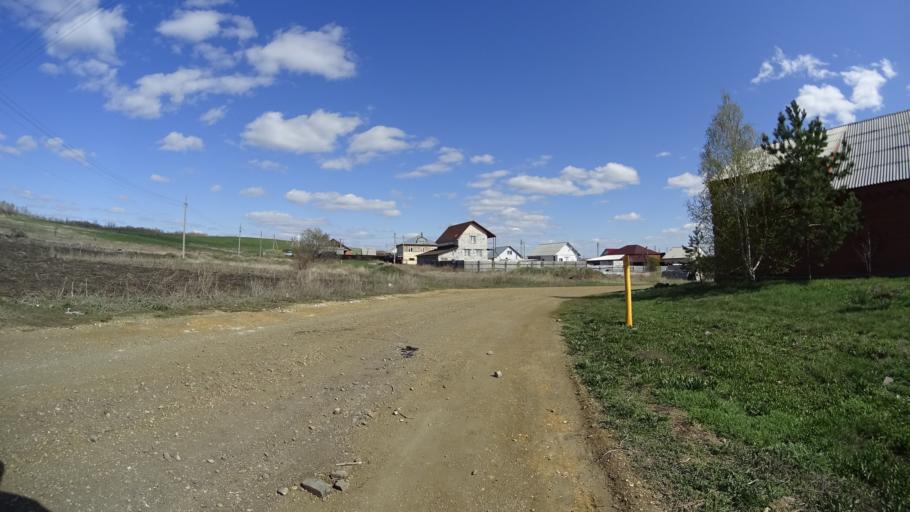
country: RU
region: Chelyabinsk
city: Troitsk
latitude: 54.0982
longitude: 61.5979
